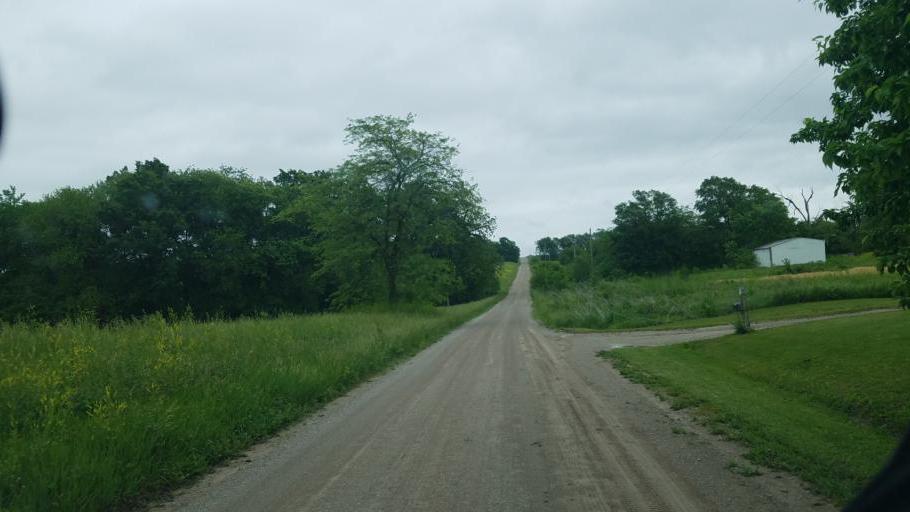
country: US
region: Missouri
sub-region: Carroll County
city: Carrollton
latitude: 39.4851
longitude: -93.5093
